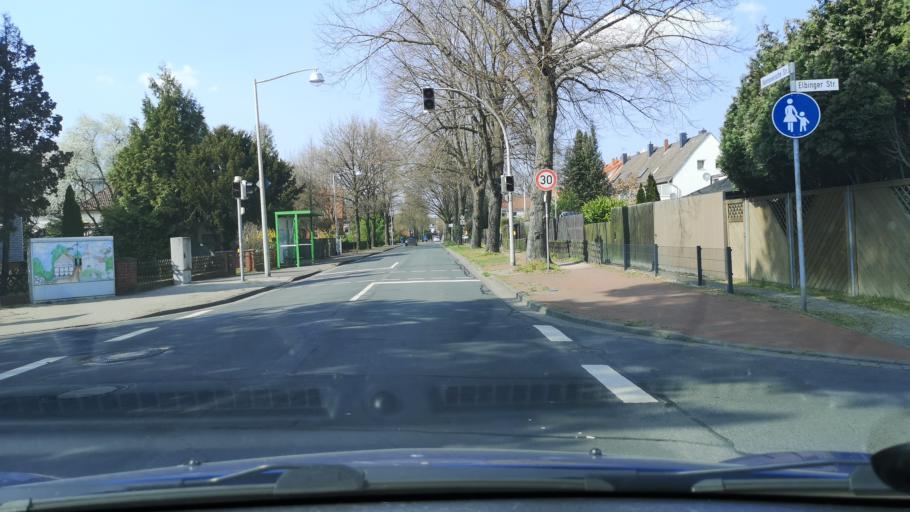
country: DE
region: Lower Saxony
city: Garbsen-Mitte
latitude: 52.4457
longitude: 9.6677
